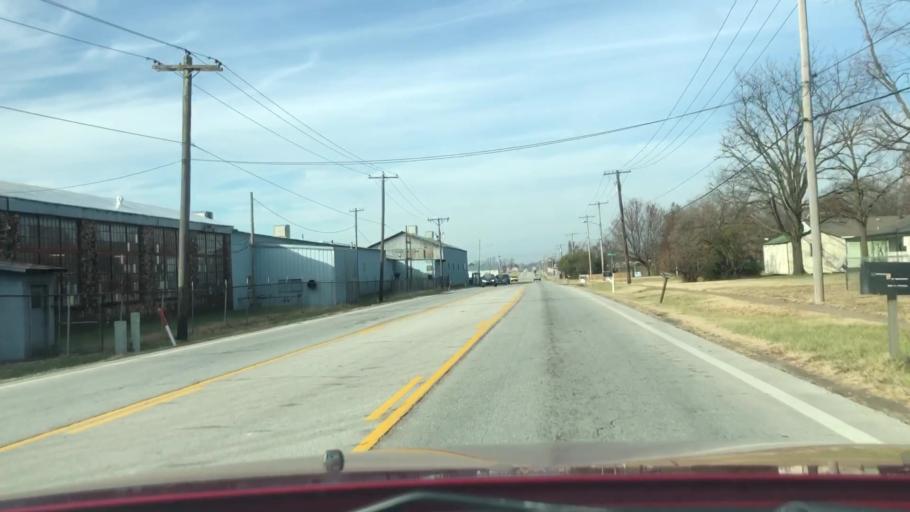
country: US
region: Missouri
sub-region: Greene County
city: Springfield
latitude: 37.2251
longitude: -93.2475
